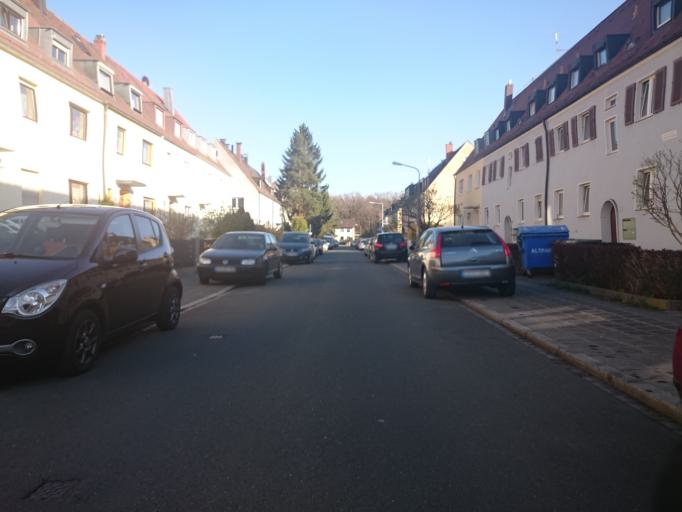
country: DE
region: Bavaria
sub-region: Regierungsbezirk Mittelfranken
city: Nuernberg
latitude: 49.4445
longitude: 11.1307
